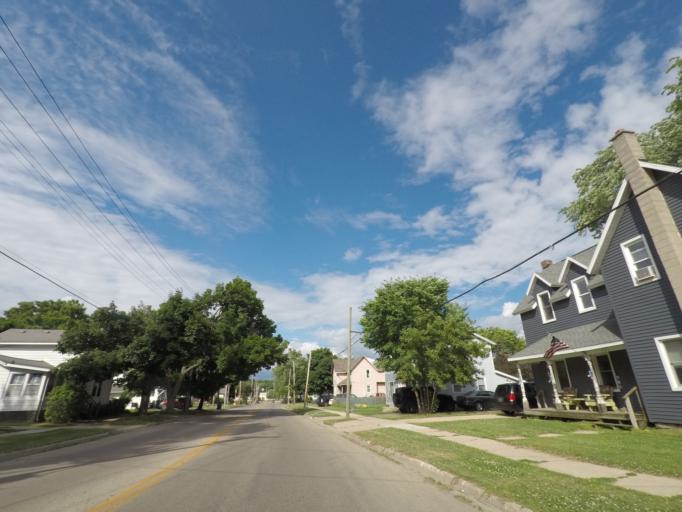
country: US
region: Wisconsin
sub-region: Rock County
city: Janesville
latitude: 42.6743
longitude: -89.0215
